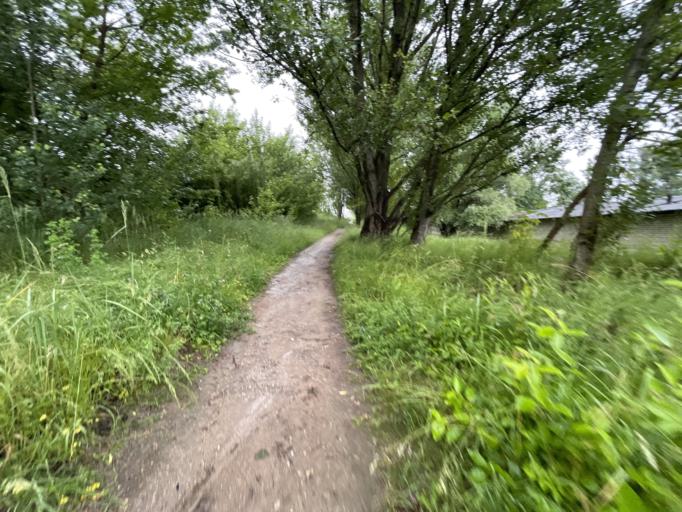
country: BY
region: Grodnenskaya
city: Hrodna
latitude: 53.7023
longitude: 23.8278
